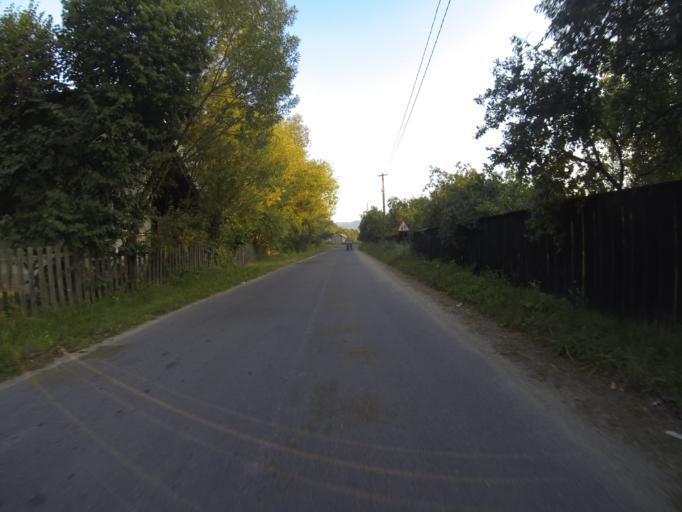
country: RO
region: Brasov
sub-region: Comuna Sinca Veche
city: Sinca Veche
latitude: 45.7617
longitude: 25.1653
